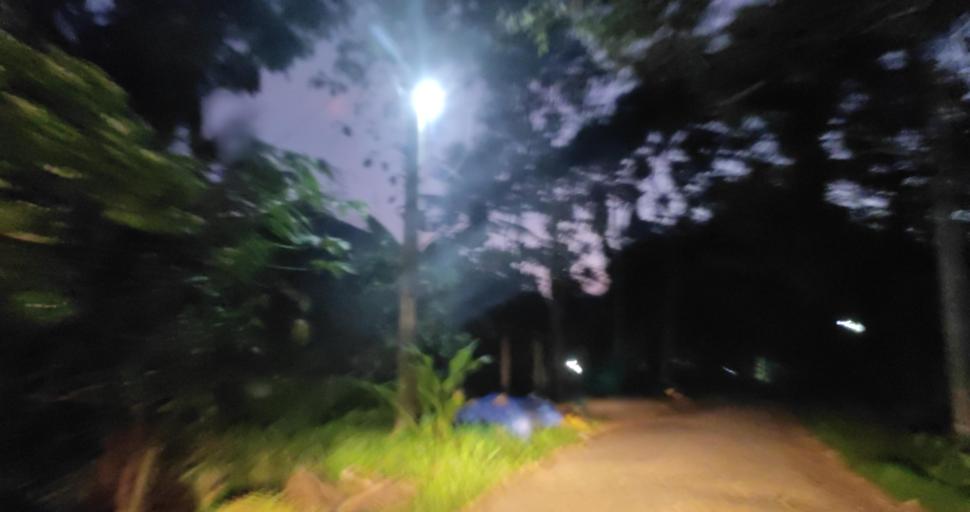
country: IN
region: Kerala
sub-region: Alappuzha
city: Shertallai
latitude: 9.6219
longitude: 76.3545
